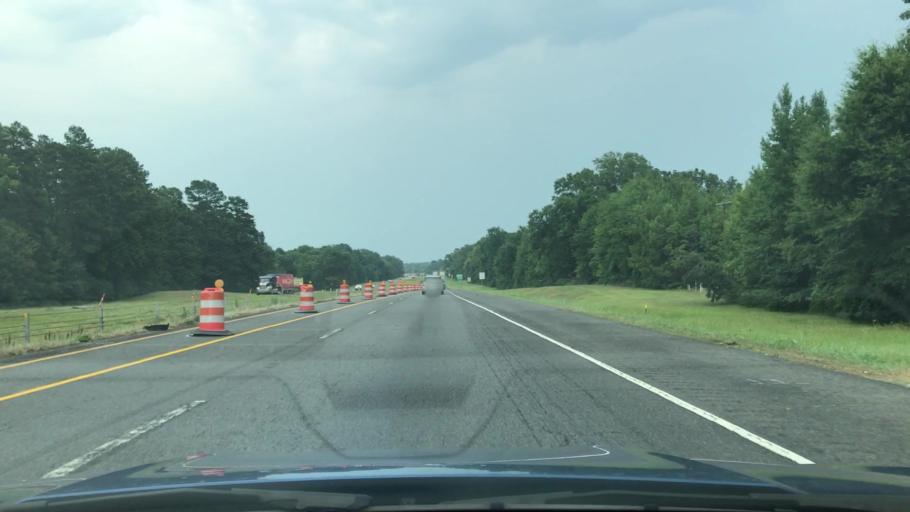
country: US
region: Texas
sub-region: Harrison County
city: Waskom
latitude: 32.4599
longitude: -94.0406
